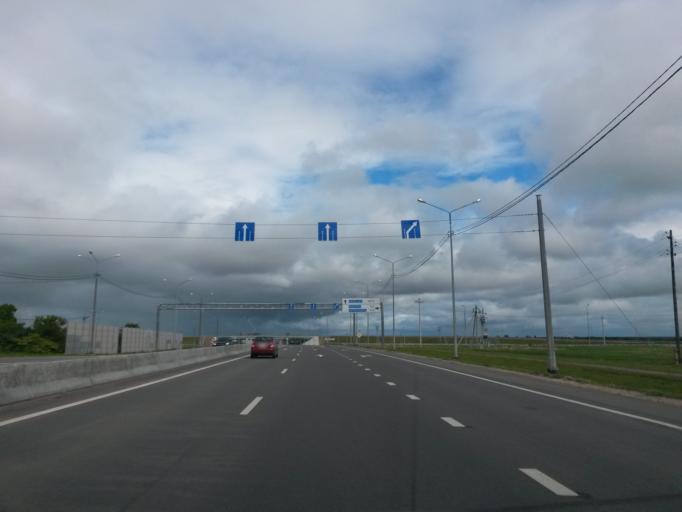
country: RU
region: Jaroslavl
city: Yaroslavl
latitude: 57.7192
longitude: 39.9026
